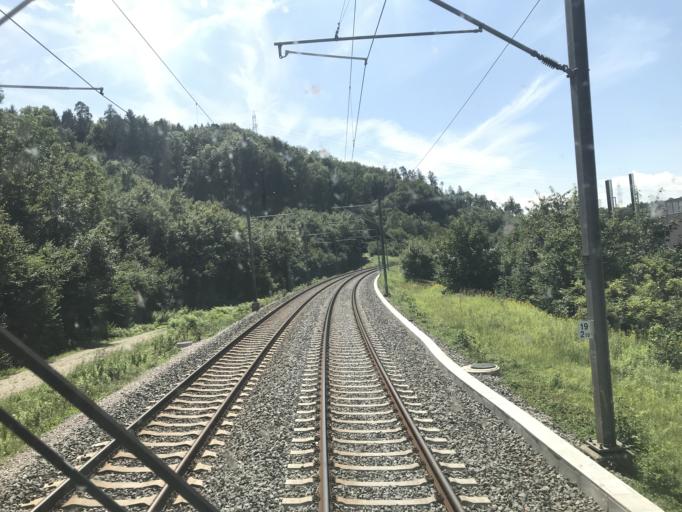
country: CH
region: Zurich
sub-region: Bezirk Pfaeffikon
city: Effretikon / Watt
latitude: 47.4412
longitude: 8.7052
